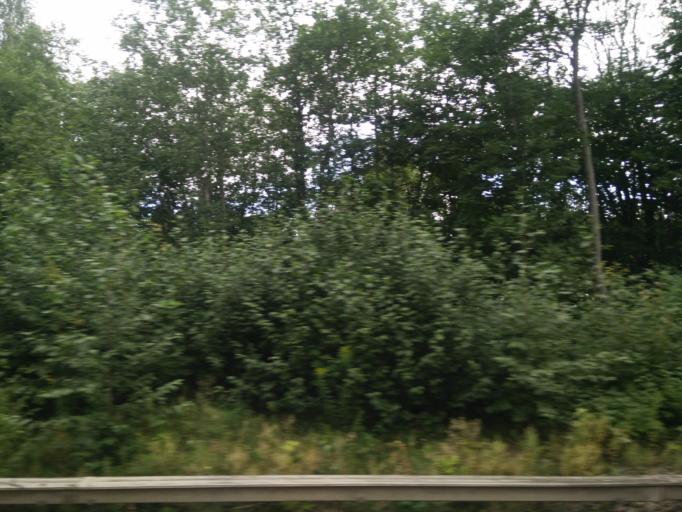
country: NO
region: Oslo
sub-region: Oslo
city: Sjolyststranda
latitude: 59.9438
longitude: 10.6722
